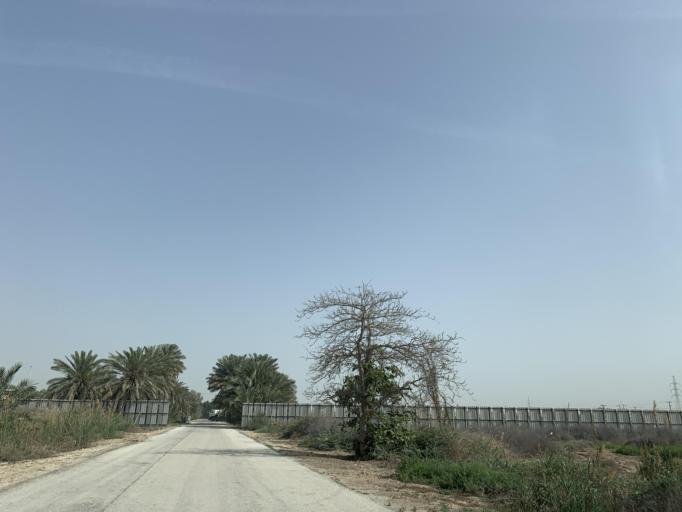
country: BH
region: Northern
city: Madinat `Isa
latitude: 26.1646
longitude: 50.5341
